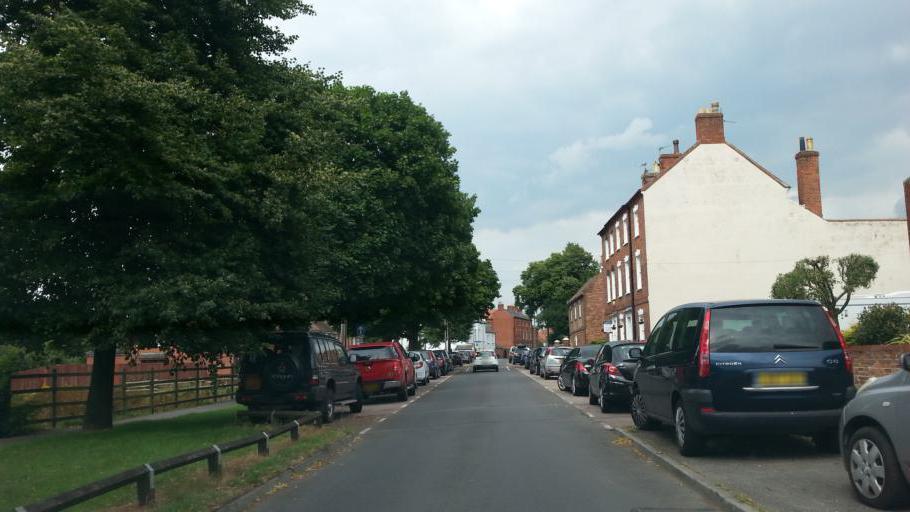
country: GB
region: England
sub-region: Nottinghamshire
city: Newark on Trent
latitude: 53.0720
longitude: -0.8197
